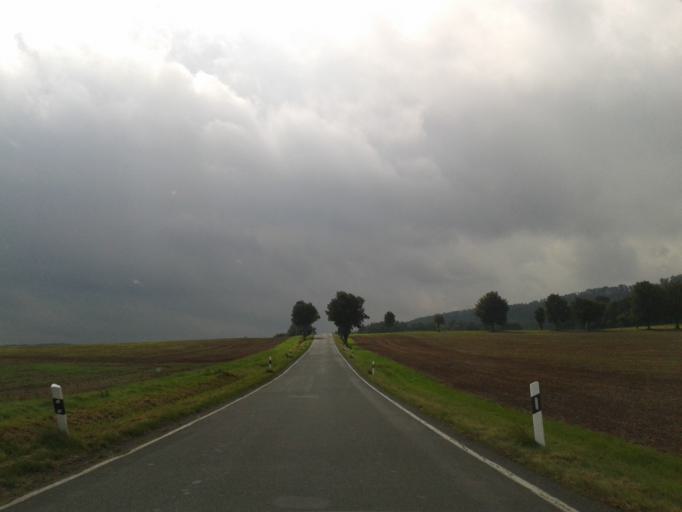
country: DE
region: North Rhine-Westphalia
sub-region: Regierungsbezirk Detmold
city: Barntrup
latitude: 51.9746
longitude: 9.1691
